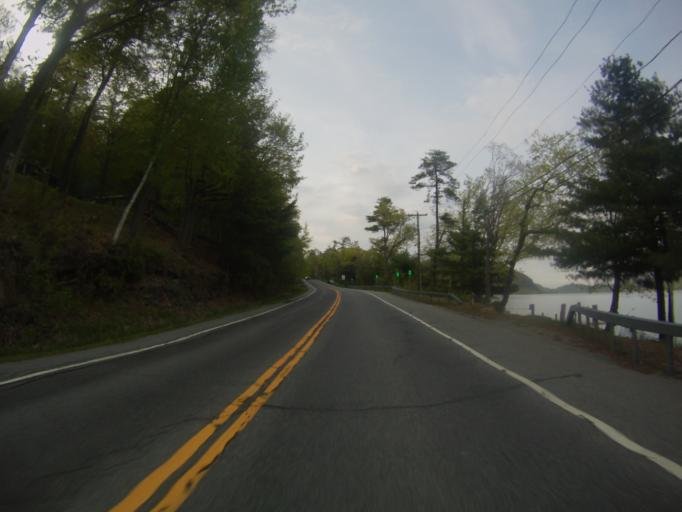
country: US
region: New York
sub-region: Essex County
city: Ticonderoga
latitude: 43.7800
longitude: -73.4876
